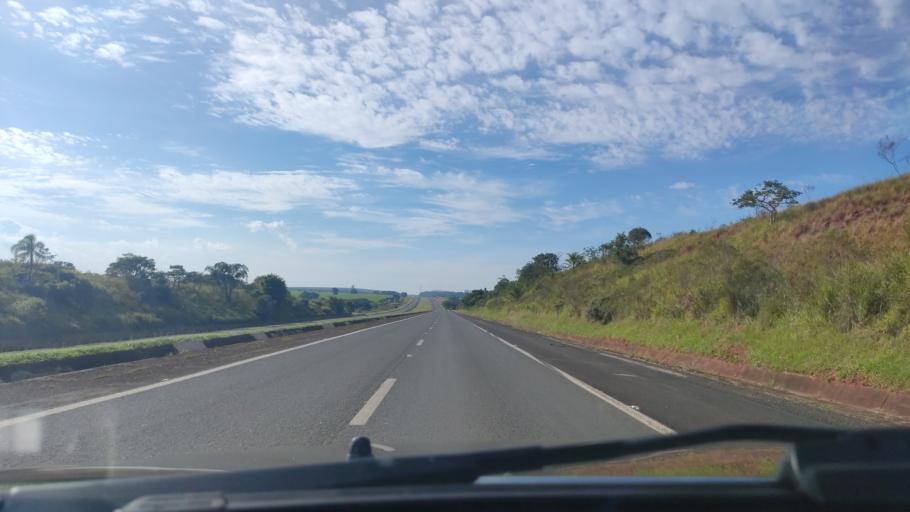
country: BR
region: Sao Paulo
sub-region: Avare
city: Avare
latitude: -22.9815
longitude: -48.7754
